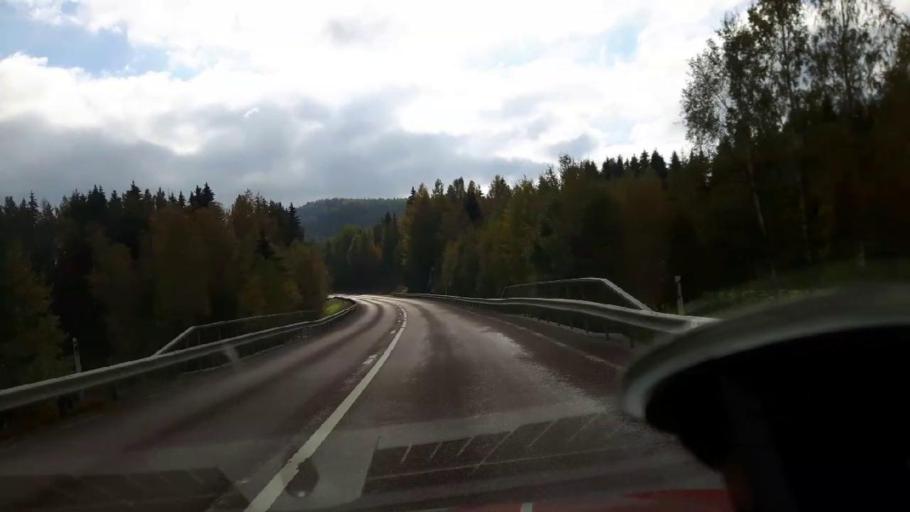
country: SE
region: Gaevleborg
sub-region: Bollnas Kommun
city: Arbra
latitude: 61.5771
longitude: 16.3167
